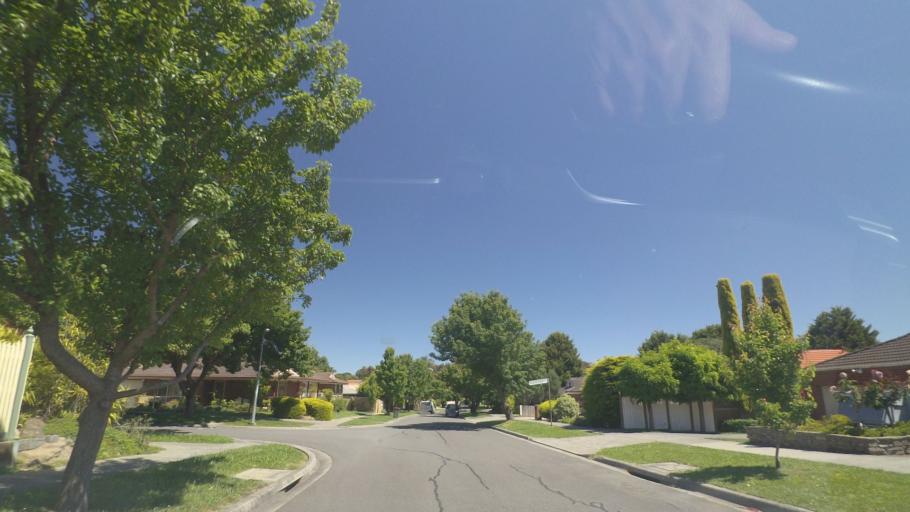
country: AU
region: Victoria
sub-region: Maroondah
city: Croydon Hills
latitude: -37.7858
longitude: 145.2654
